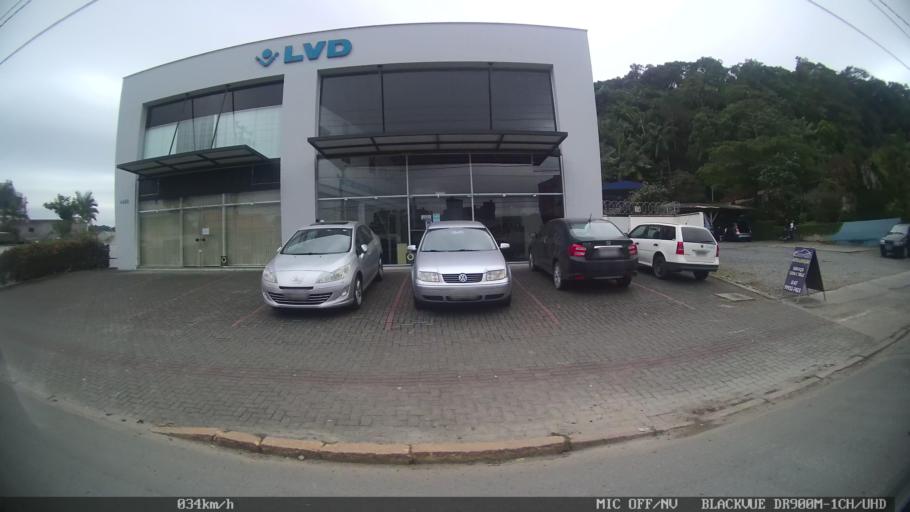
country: BR
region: Santa Catarina
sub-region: Joinville
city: Joinville
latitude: -26.2691
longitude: -48.8546
